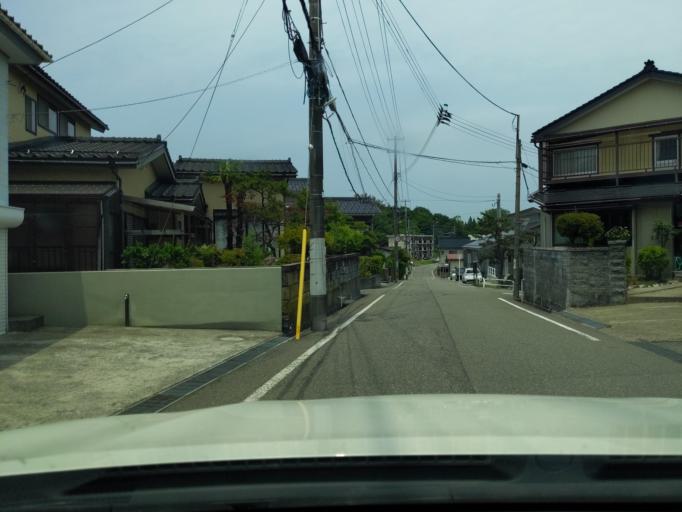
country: JP
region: Niigata
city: Kashiwazaki
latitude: 37.3542
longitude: 138.5410
